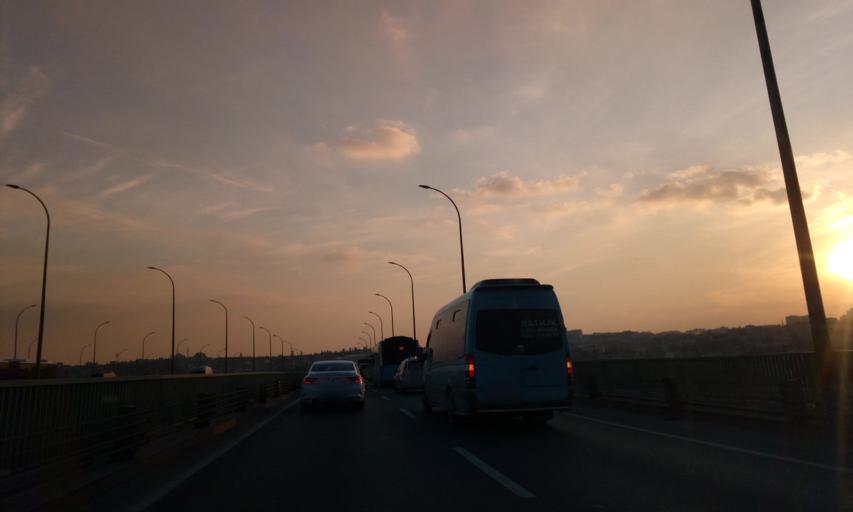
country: TR
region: Istanbul
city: Istanbul
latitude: 41.0453
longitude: 28.9429
